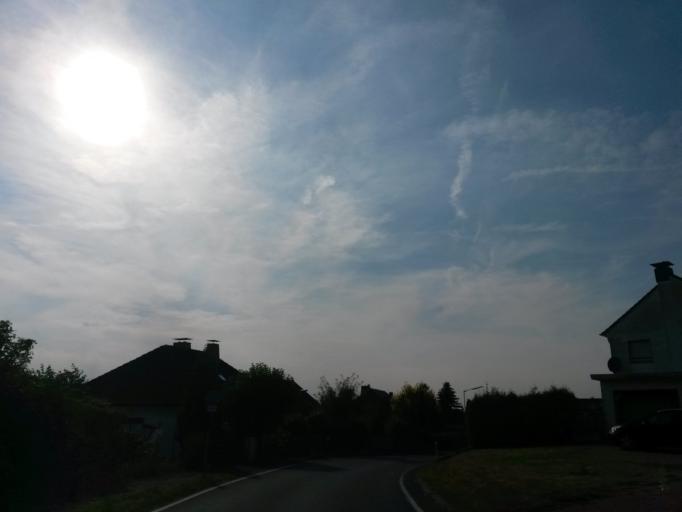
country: DE
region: North Rhine-Westphalia
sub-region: Regierungsbezirk Koln
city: Overath
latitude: 50.9413
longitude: 7.3437
